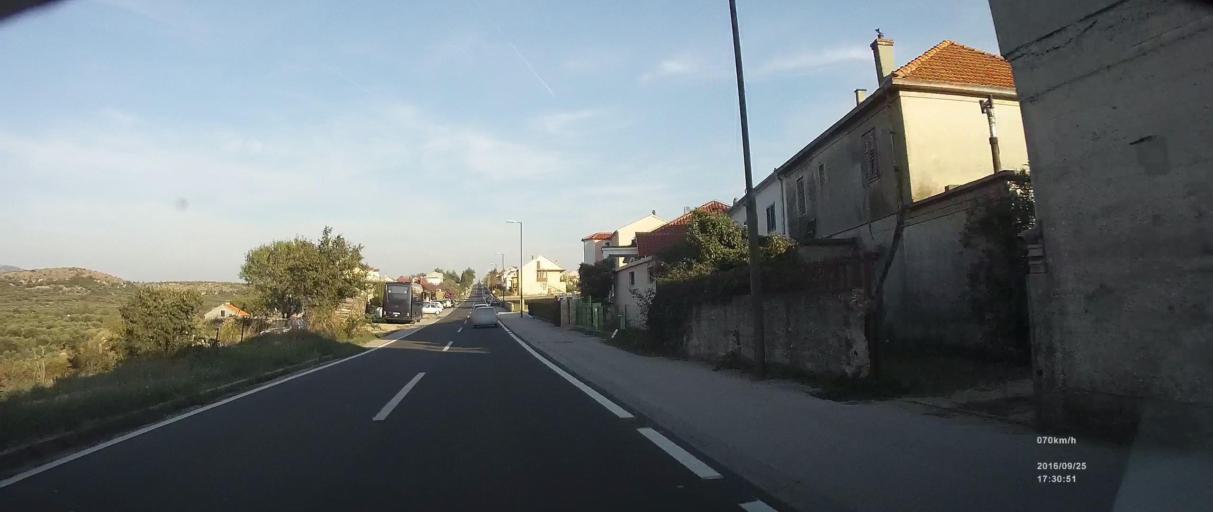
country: HR
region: Sibensko-Kniniska
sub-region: Grad Sibenik
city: Brodarica
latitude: 43.6795
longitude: 15.9823
